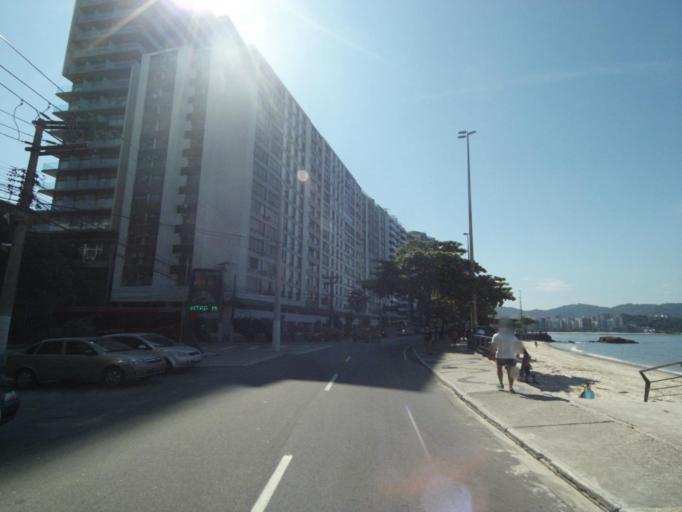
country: BR
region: Rio de Janeiro
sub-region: Niteroi
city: Niteroi
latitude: -22.9050
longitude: -43.1227
